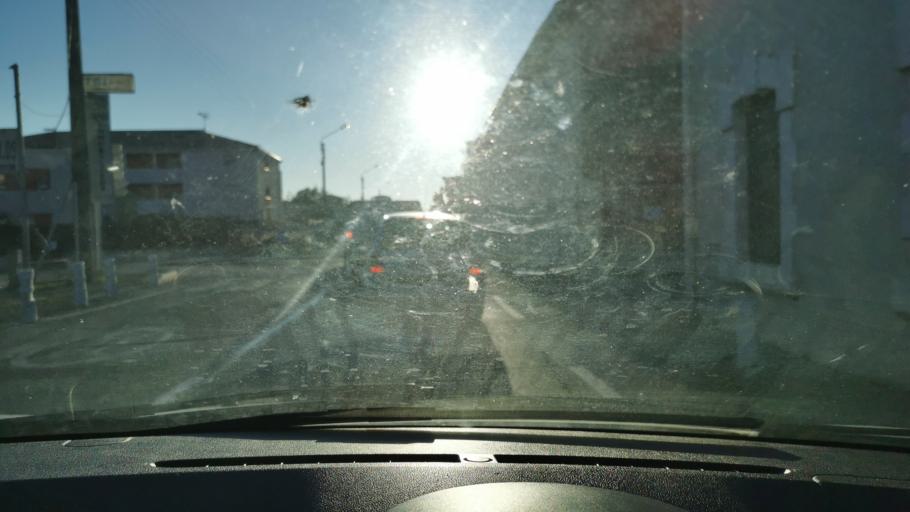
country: FR
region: Languedoc-Roussillon
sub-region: Departement de l'Herault
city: Frontignan
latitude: 43.4428
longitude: 3.7489
